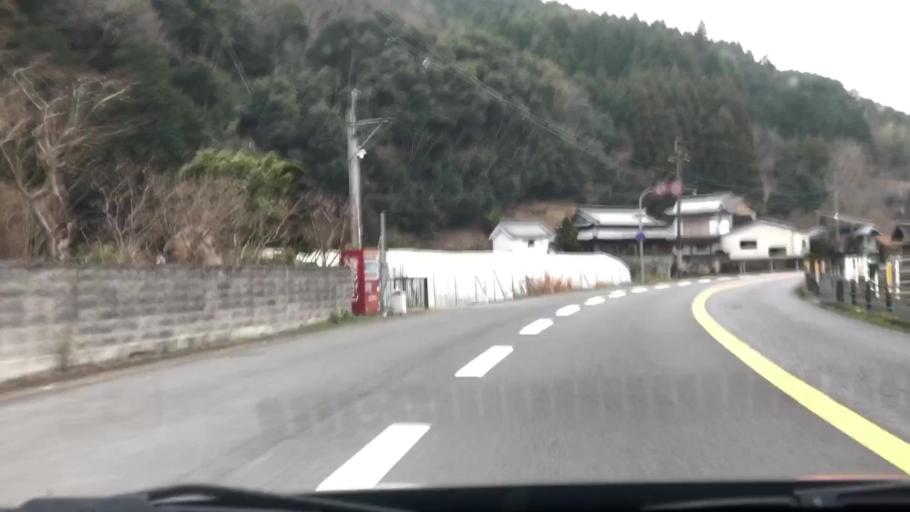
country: JP
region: Oita
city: Usuki
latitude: 33.0076
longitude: 131.7399
